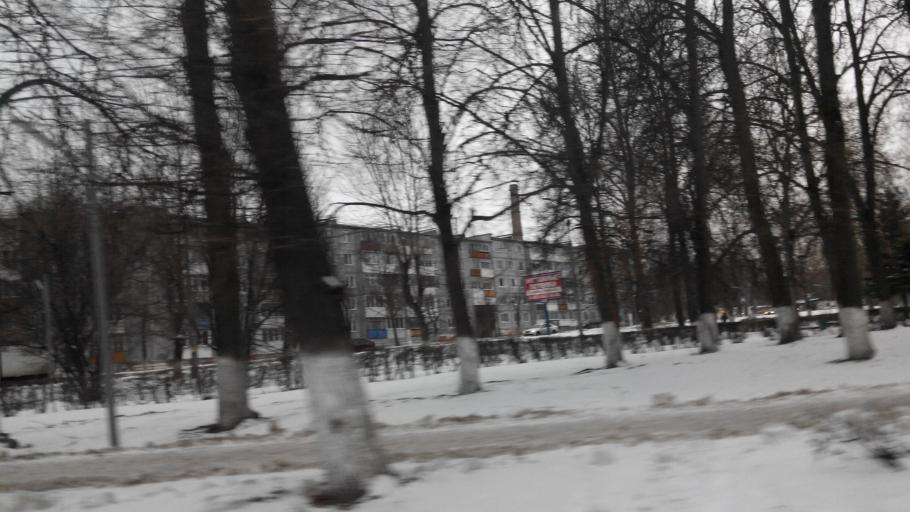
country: RU
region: Tula
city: Uzlovaya
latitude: 53.9695
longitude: 38.1663
